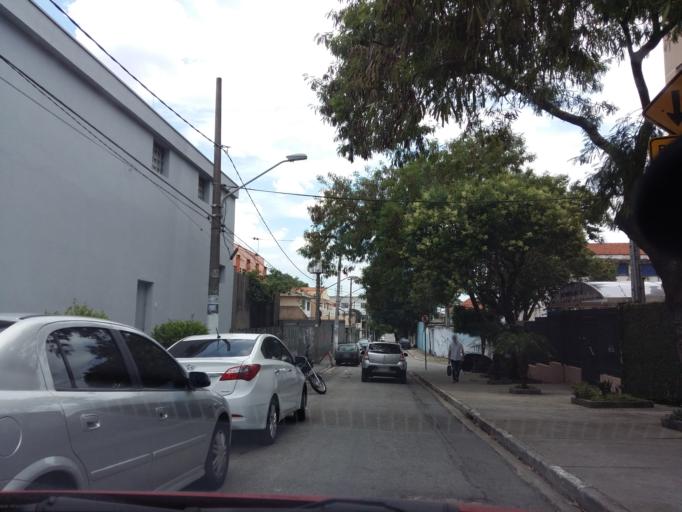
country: BR
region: Sao Paulo
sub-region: Sao Caetano Do Sul
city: Sao Caetano do Sul
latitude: -23.6320
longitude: -46.6015
